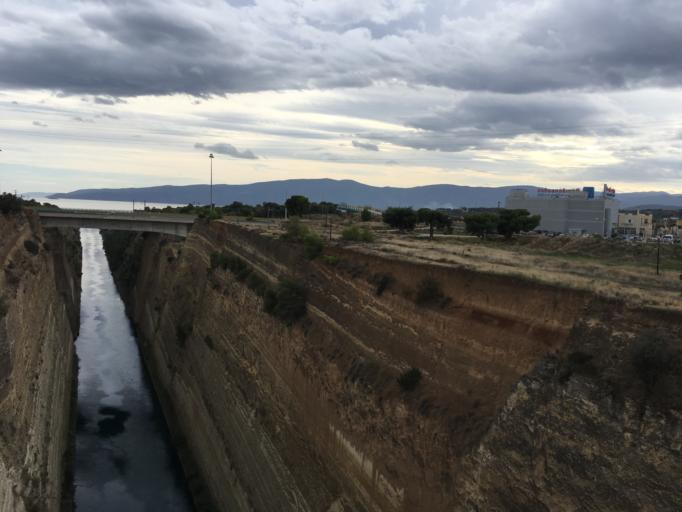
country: GR
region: Peloponnese
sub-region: Nomos Korinthias
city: Kyras Vrysi
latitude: 37.9270
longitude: 22.9948
